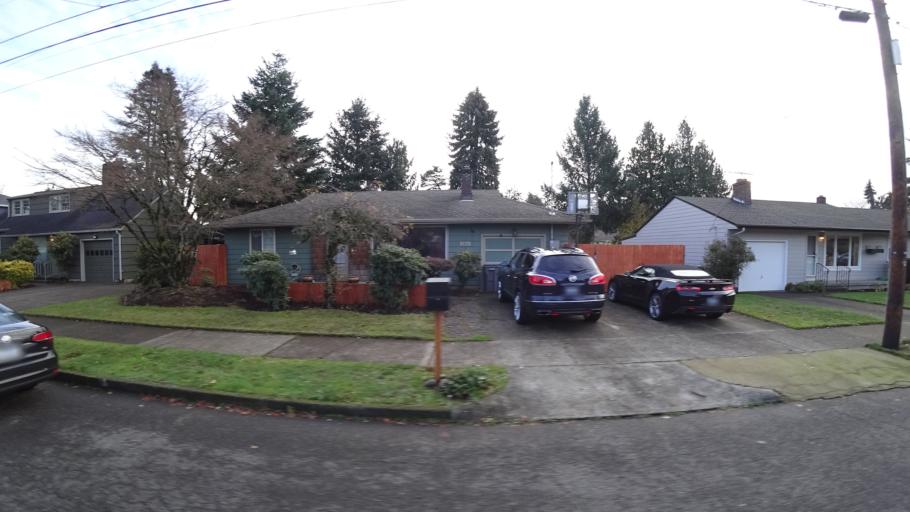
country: US
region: Oregon
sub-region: Multnomah County
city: Lents
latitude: 45.5147
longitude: -122.5341
